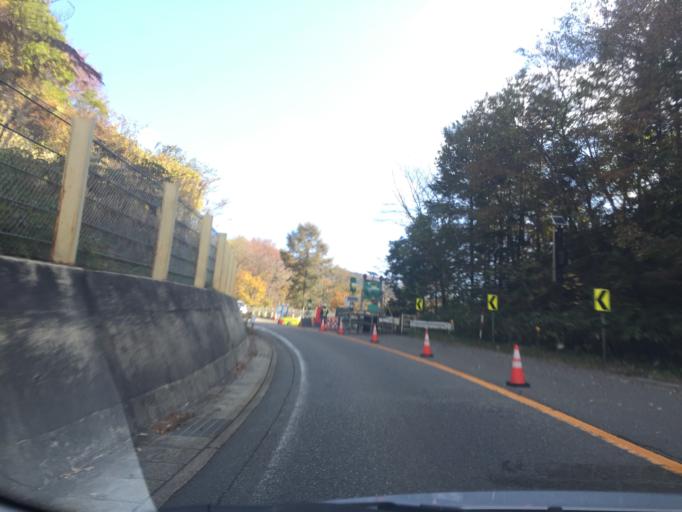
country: JP
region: Gifu
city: Nakatsugawa
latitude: 35.3431
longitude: 137.6536
